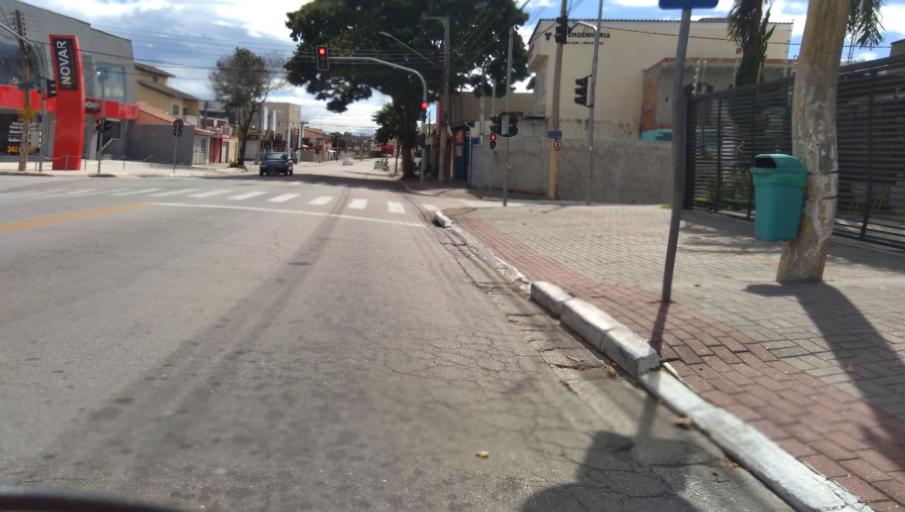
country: BR
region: Sao Paulo
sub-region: Sao Jose Dos Campos
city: Sao Jose dos Campos
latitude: -23.1744
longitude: -45.8530
